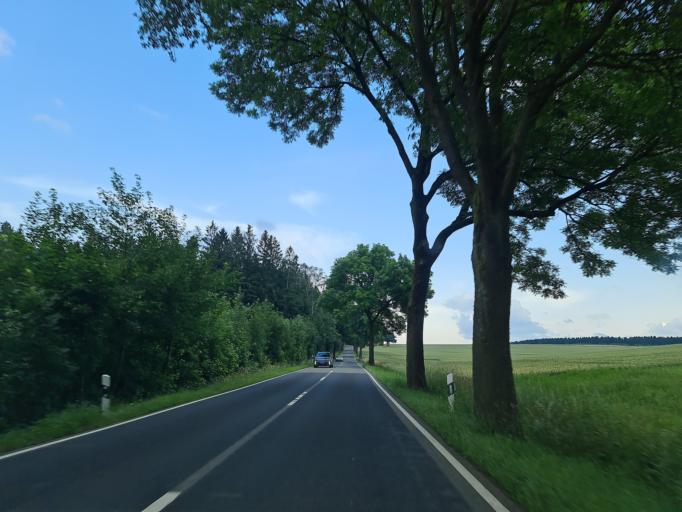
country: DE
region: Saxony
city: Neustadt Vogtland
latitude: 50.4583
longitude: 12.3078
